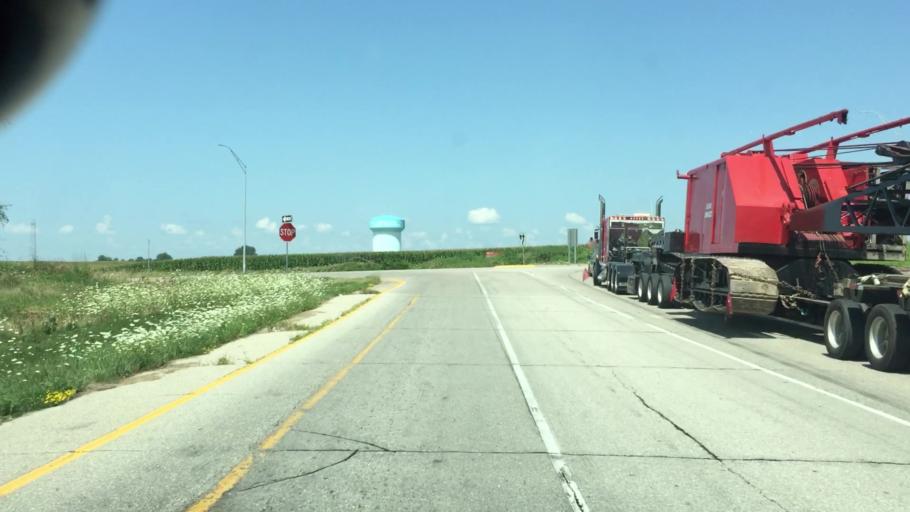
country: US
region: Iowa
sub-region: Jasper County
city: Newton
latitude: 41.6842
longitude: -92.9992
